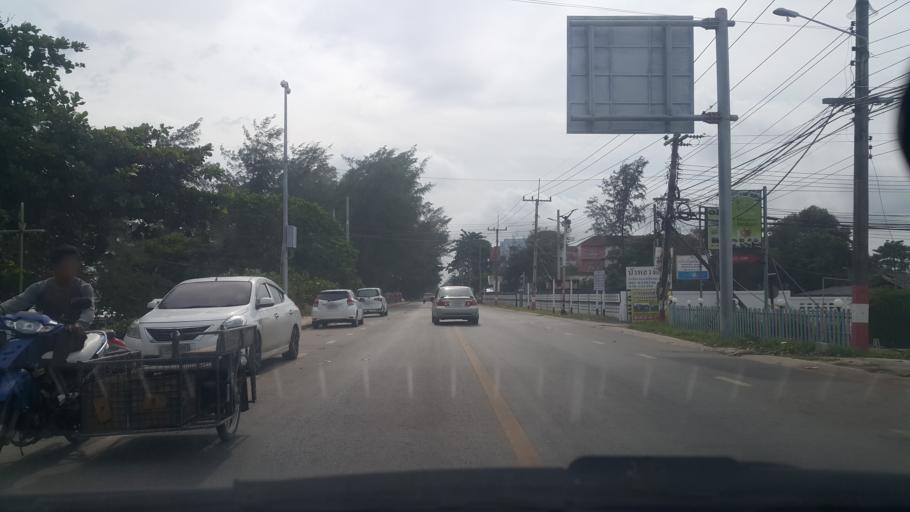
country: TH
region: Rayong
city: Rayong
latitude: 12.6277
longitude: 101.3522
